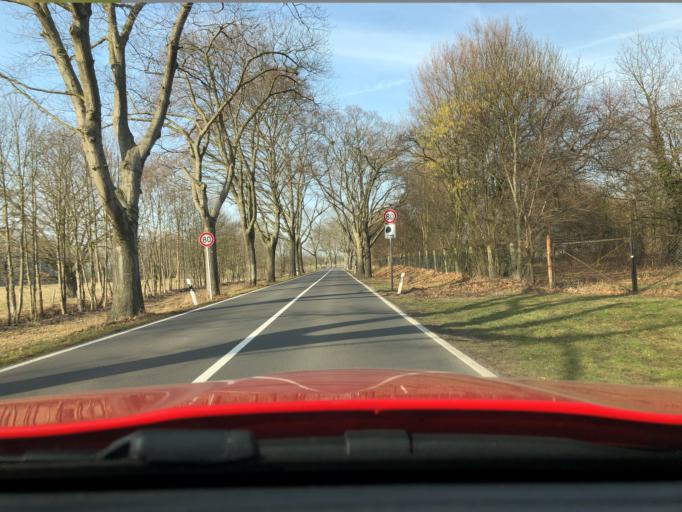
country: DE
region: Brandenburg
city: Neuhardenberg
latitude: 52.5134
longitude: 14.2285
